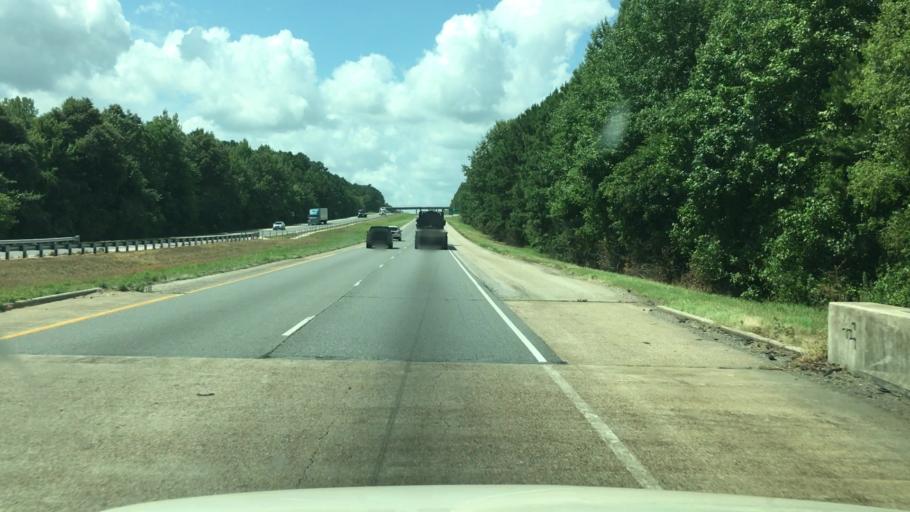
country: US
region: Arkansas
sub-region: Clark County
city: Arkadelphia
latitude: 34.0799
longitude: -93.1161
